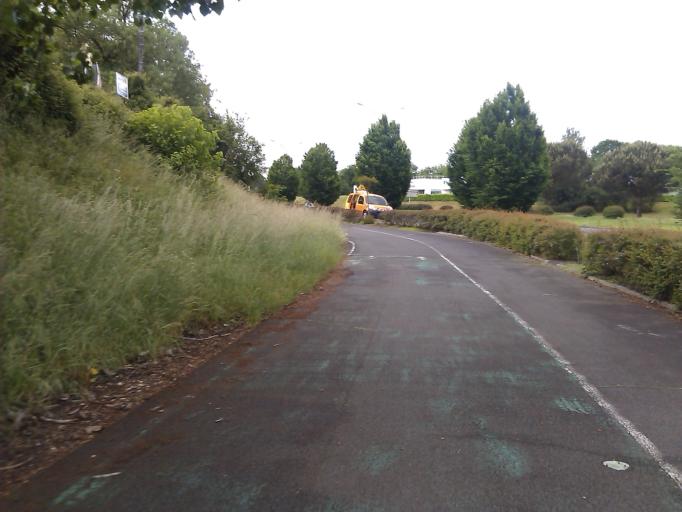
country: FR
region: Aquitaine
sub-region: Departement de la Gironde
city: Cestas
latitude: 44.7554
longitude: -0.6853
